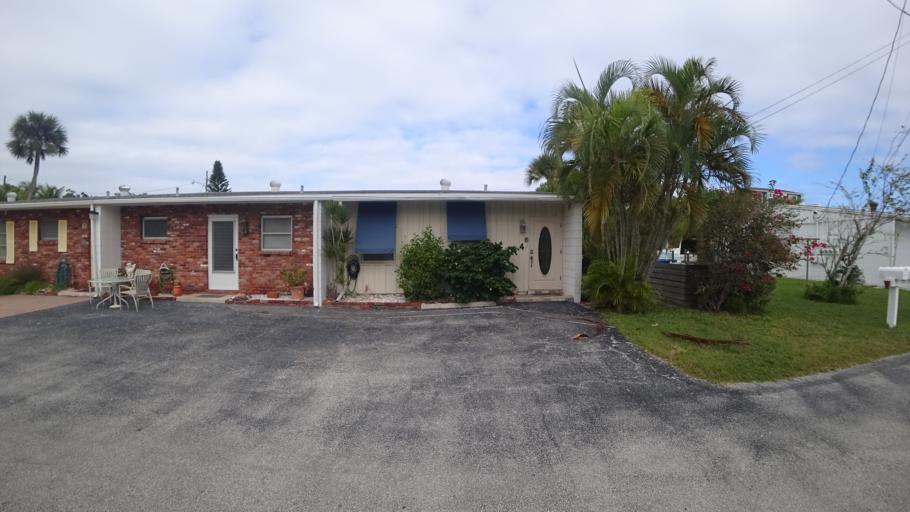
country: US
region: Florida
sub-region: Manatee County
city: Longboat Key
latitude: 27.4157
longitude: -82.6575
